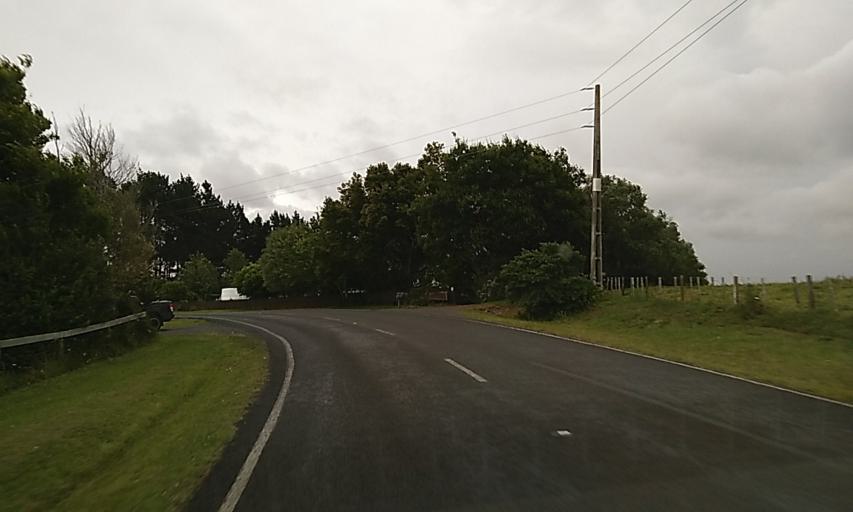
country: NZ
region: Auckland
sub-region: Auckland
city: Pukekohe East
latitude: -37.3228
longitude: 174.9189
